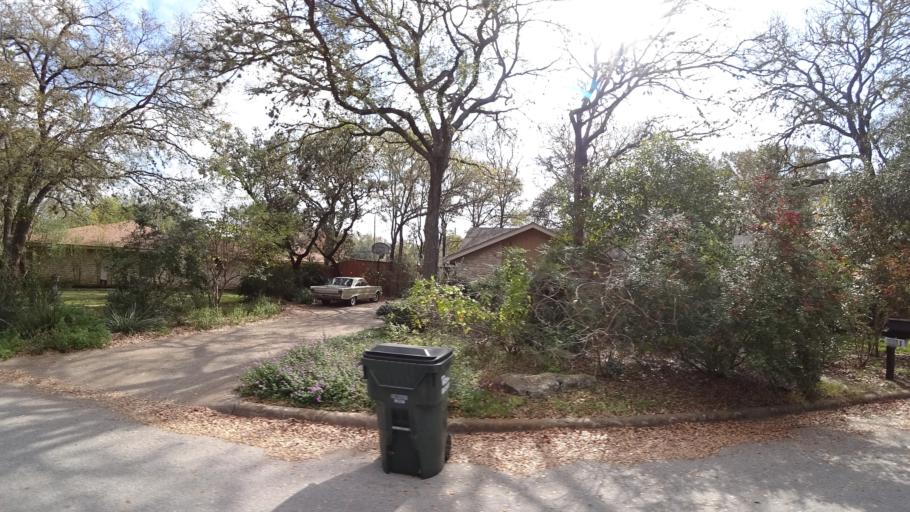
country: US
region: Texas
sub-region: Travis County
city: Shady Hollow
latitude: 30.1737
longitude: -97.8570
